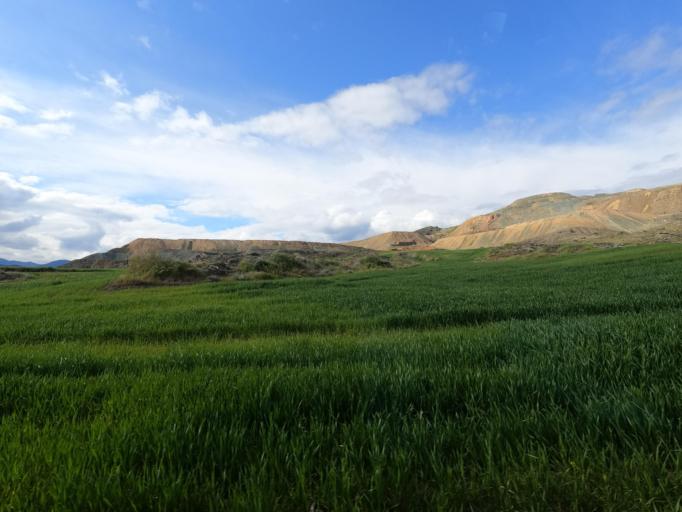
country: CY
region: Lefkosia
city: Lefka
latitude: 35.0981
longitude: 32.9056
